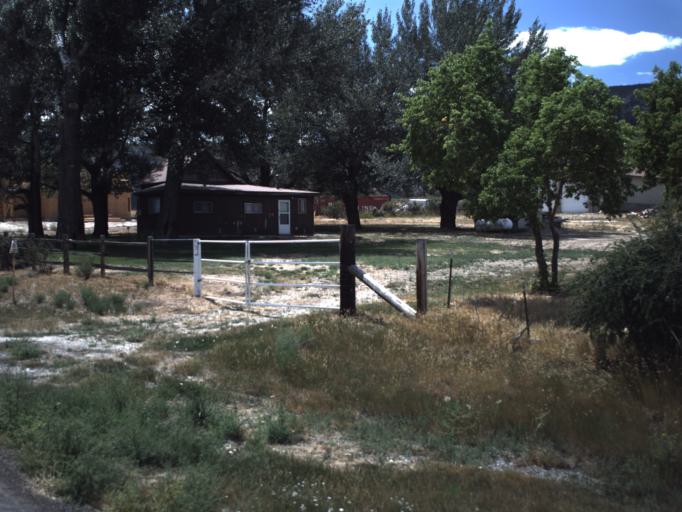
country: US
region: Utah
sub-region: Sanpete County
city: Moroni
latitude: 39.4886
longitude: -111.6389
